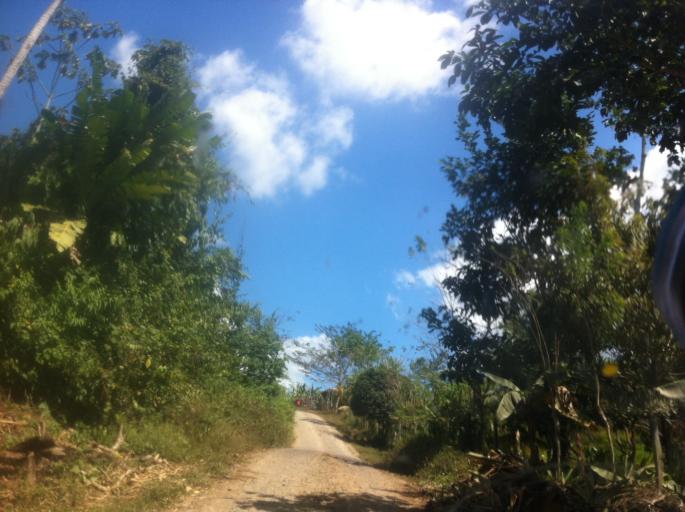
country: CR
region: Alajuela
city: Los Chiles
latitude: 11.2340
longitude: -84.4869
